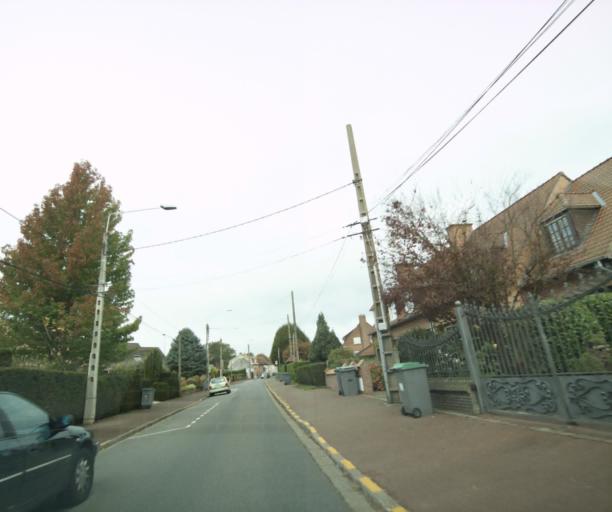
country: FR
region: Nord-Pas-de-Calais
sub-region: Departement du Nord
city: Roncq
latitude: 50.7511
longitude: 3.1293
